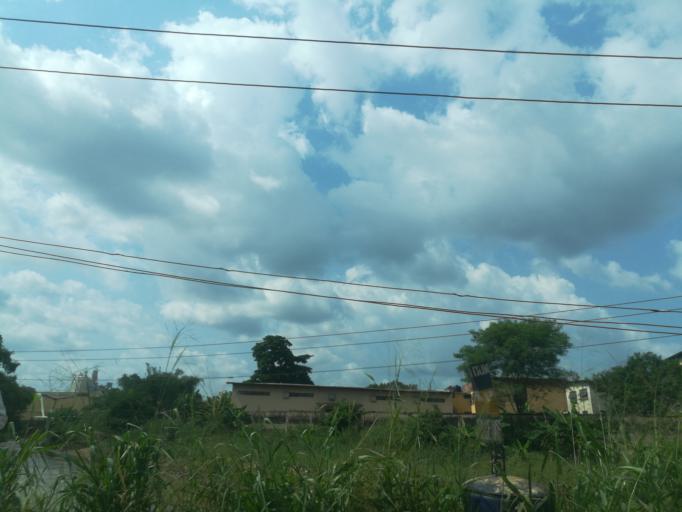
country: NG
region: Oyo
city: Ibadan
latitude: 7.3601
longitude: 3.8520
